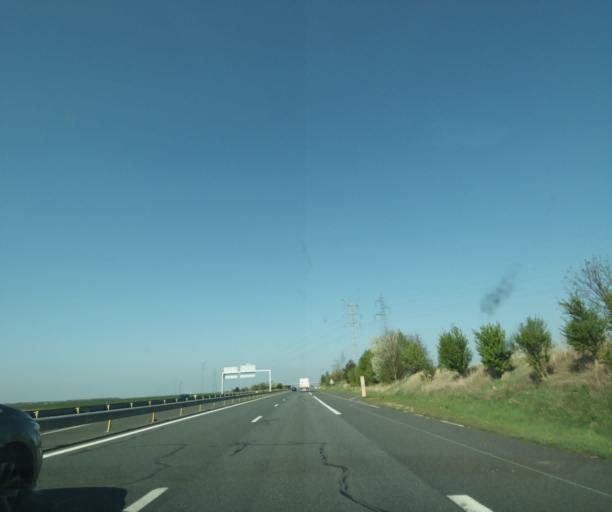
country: FR
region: Centre
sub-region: Departement du Loiret
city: Corquilleroy
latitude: 48.0700
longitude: 2.6759
